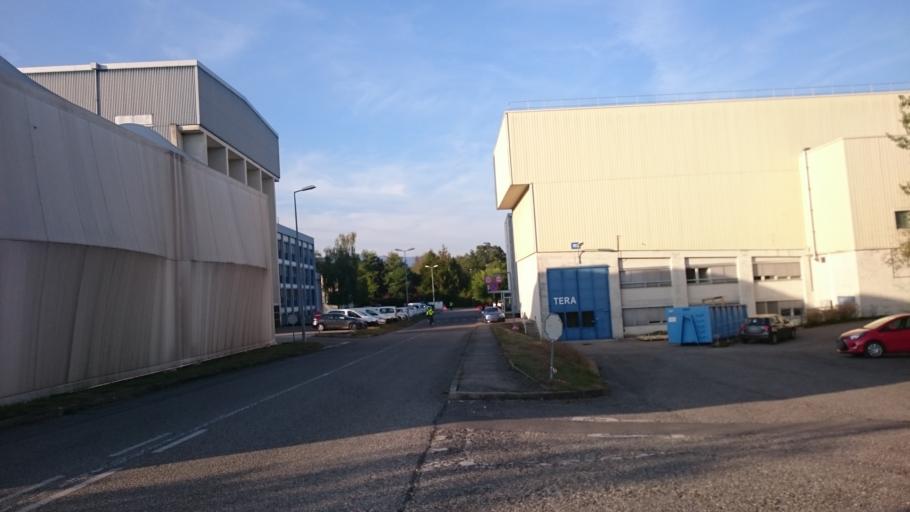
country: FR
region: Rhone-Alpes
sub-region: Departement de l'Ain
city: Saint-Genis-Pouilly
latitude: 46.2375
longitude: 6.0360
